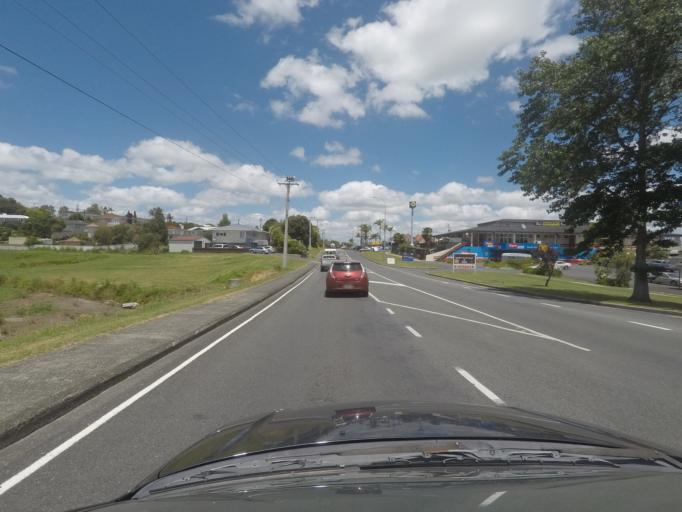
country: NZ
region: Northland
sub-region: Whangarei
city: Whangarei
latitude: -35.7532
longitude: 174.3682
